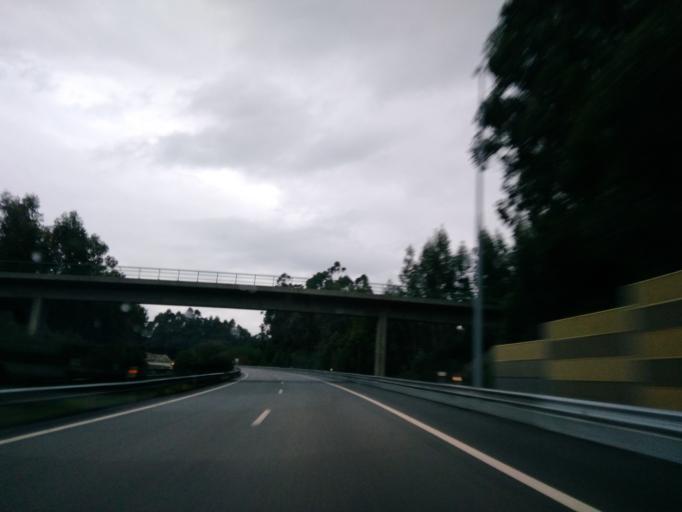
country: PT
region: Braga
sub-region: Vila Nova de Famalicao
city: Vila Nova de Famalicao
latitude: 41.4043
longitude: -8.4931
